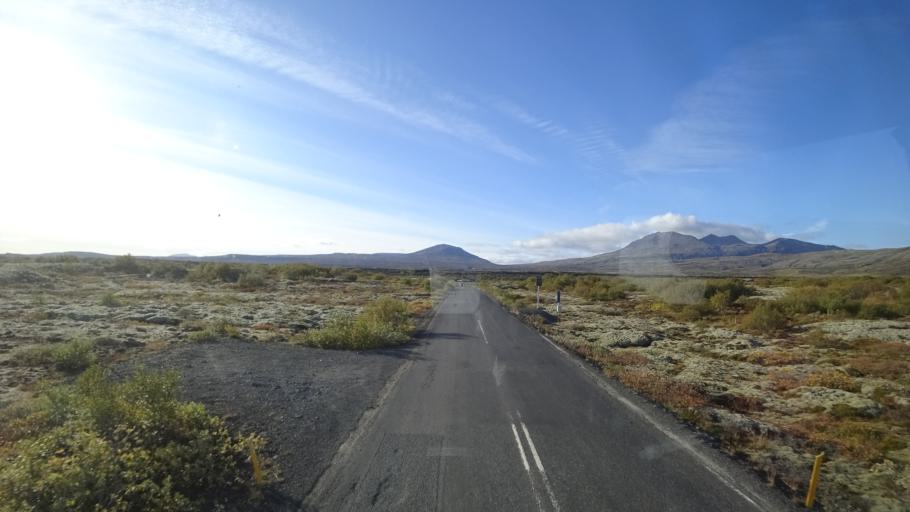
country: IS
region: South
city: Hveragerdi
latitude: 64.2780
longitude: -21.0787
